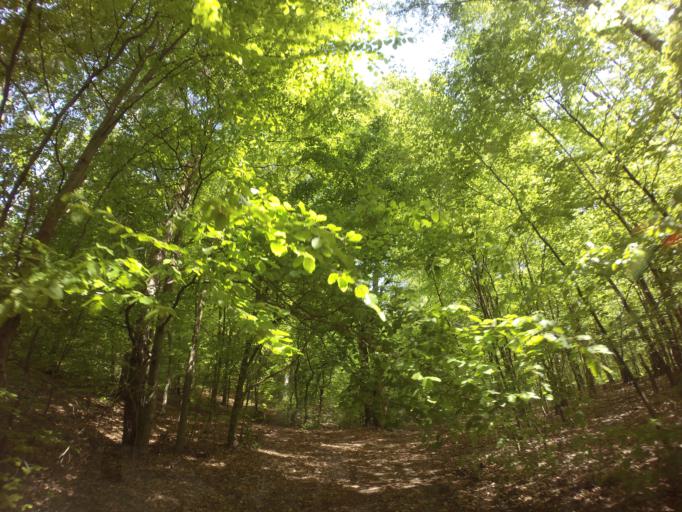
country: PL
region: West Pomeranian Voivodeship
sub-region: Powiat choszczenski
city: Pelczyce
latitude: 52.9487
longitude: 15.3333
